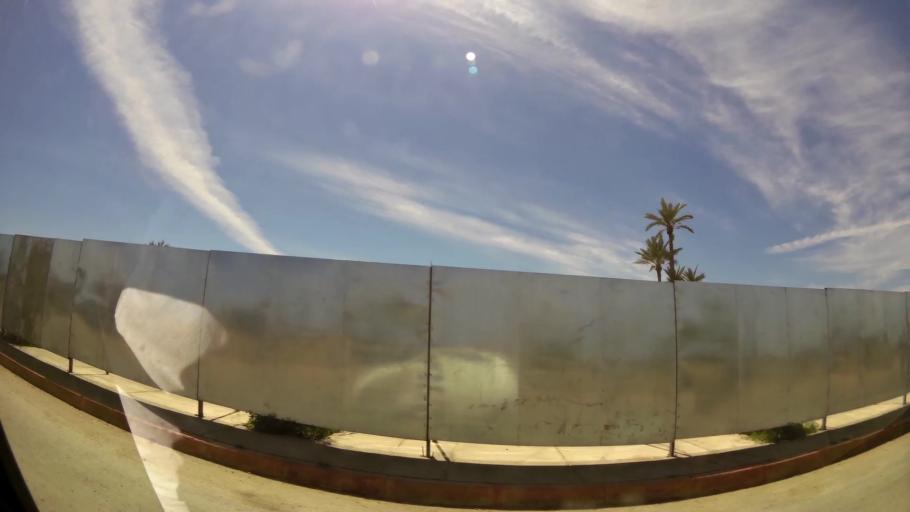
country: MA
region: Marrakech-Tensift-Al Haouz
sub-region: Marrakech
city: Marrakesh
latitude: 31.6704
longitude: -7.9976
